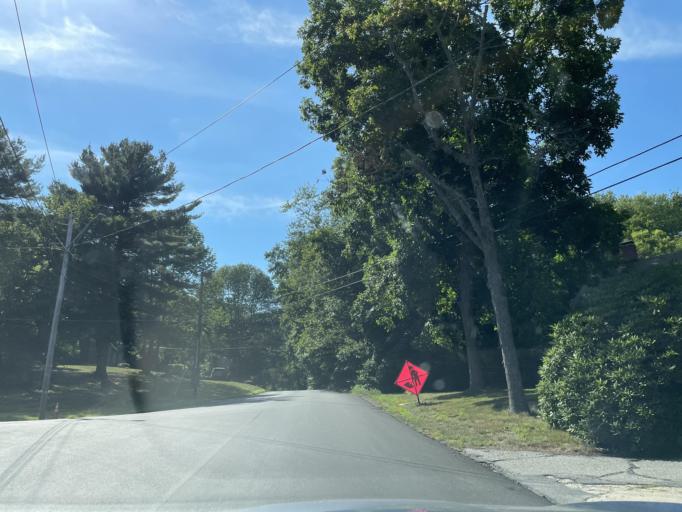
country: US
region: Massachusetts
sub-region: Worcester County
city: Northbridge
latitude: 42.1243
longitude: -71.6115
